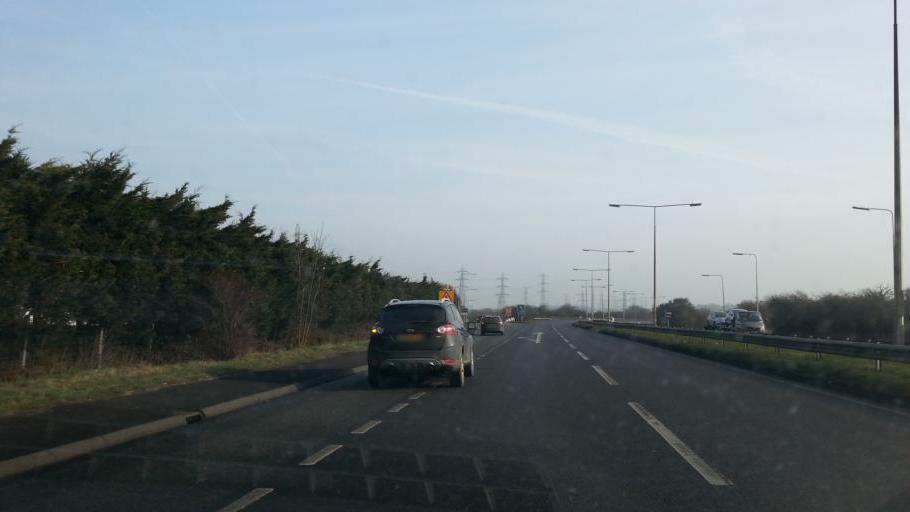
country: GB
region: England
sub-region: Essex
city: South Benfleet
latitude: 51.5882
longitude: 0.5636
